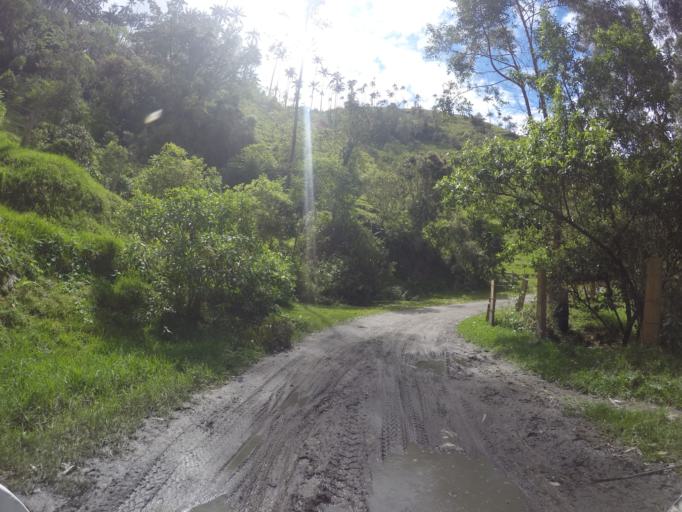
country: CO
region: Tolima
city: Cajamarca
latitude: 4.5297
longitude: -75.4553
